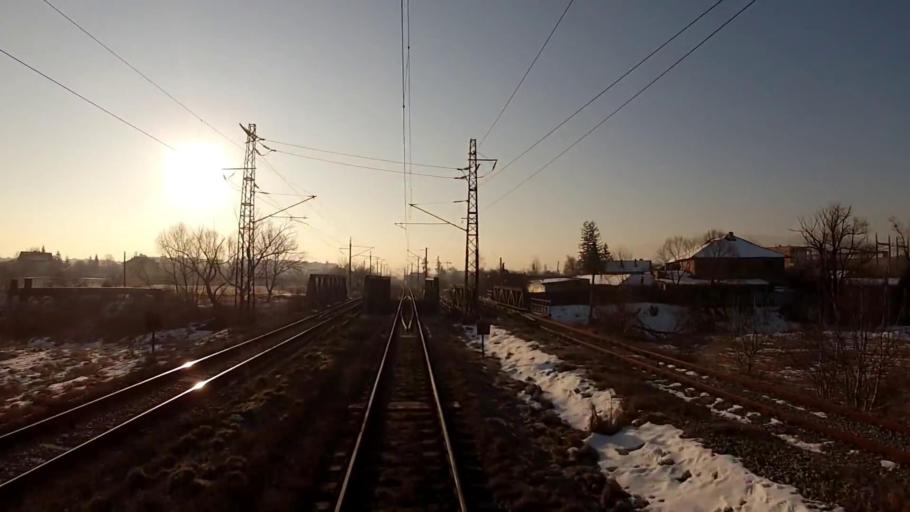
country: BG
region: Sofiya
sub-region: Obshtina Bozhurishte
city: Bozhurishte
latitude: 42.7488
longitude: 23.2519
